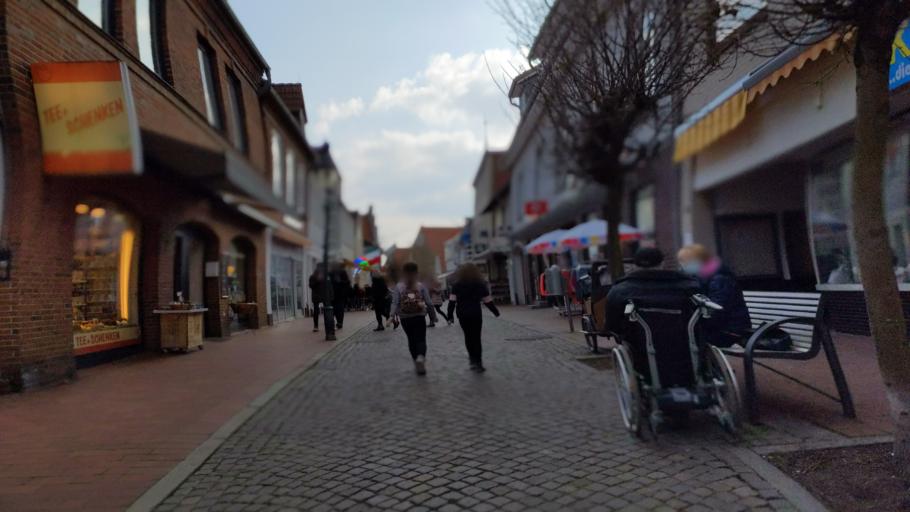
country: DE
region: Schleswig-Holstein
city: Neustadt in Holstein
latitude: 54.1088
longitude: 10.8158
